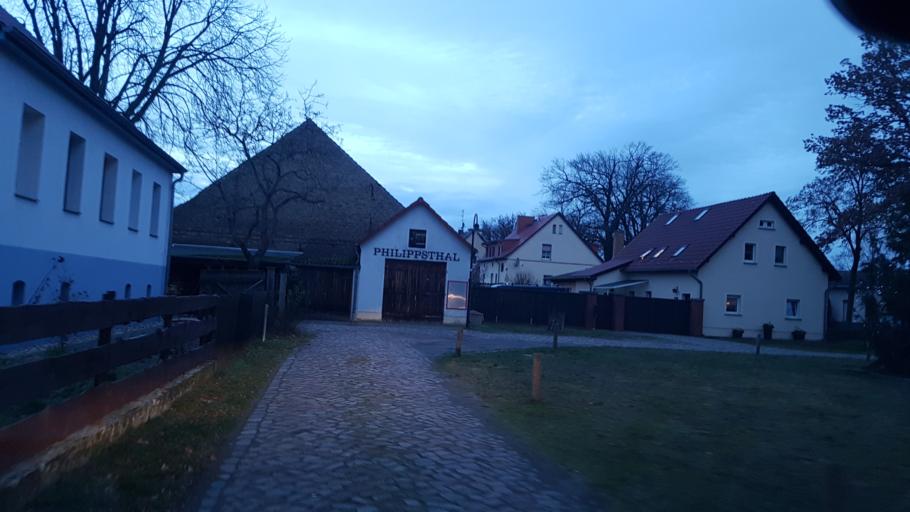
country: DE
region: Berlin
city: Wannsee
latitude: 52.3332
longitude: 13.1406
